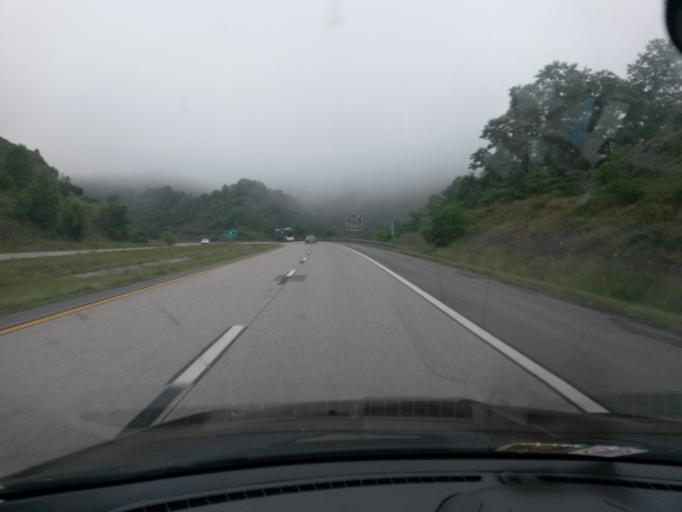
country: US
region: West Virginia
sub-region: Summers County
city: Hinton
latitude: 37.7859
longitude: -80.8845
